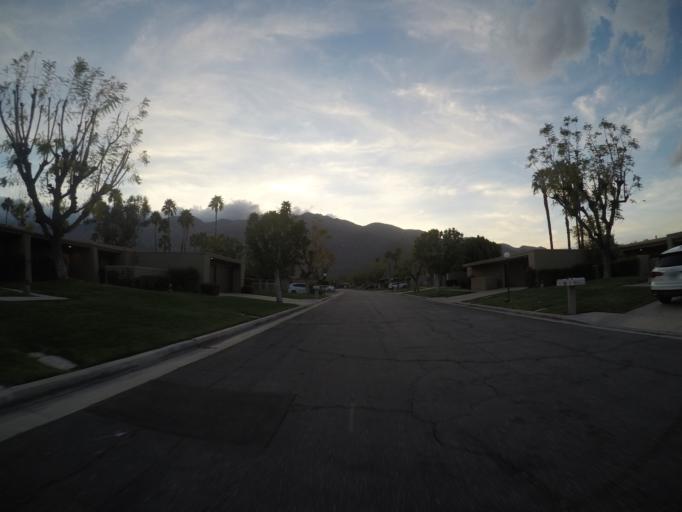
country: US
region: California
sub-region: Riverside County
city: Palm Springs
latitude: 33.8190
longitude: -116.5334
